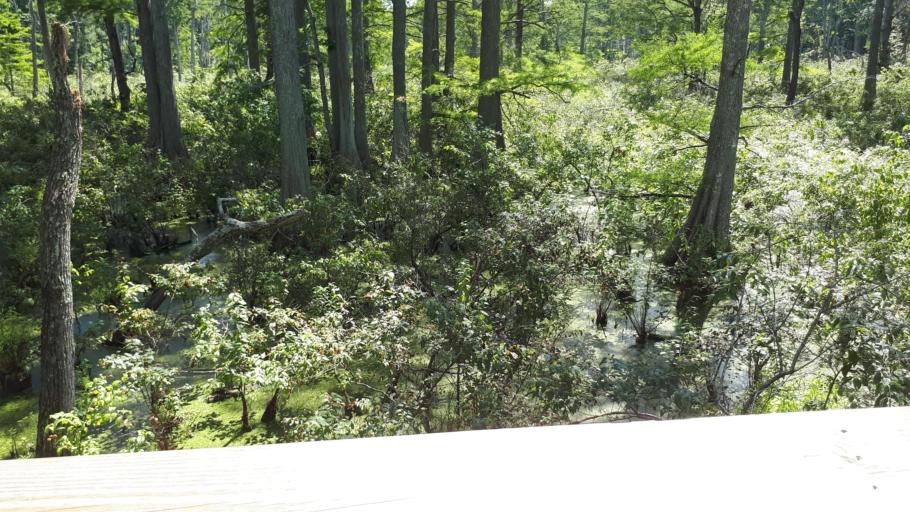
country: US
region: Kentucky
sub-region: Union County
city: Uniontown
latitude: 37.8311
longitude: -87.9953
